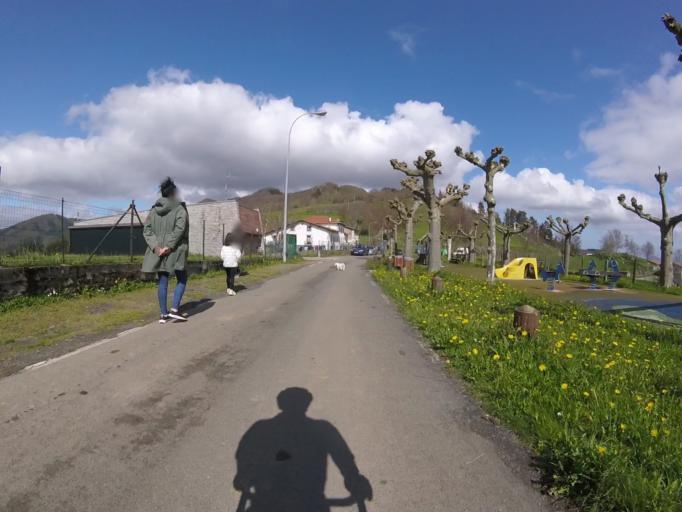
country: ES
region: Basque Country
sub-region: Provincia de Guipuzcoa
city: Albiztur
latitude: 43.1342
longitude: -2.1079
